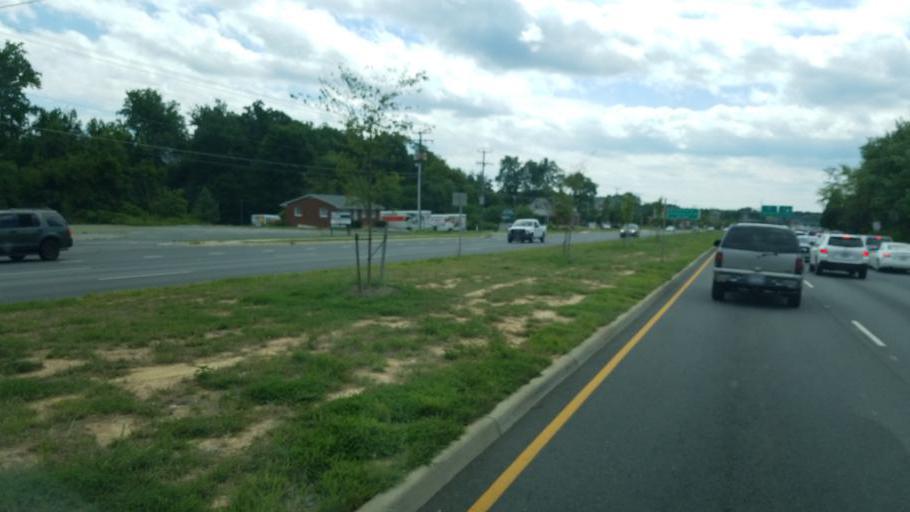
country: US
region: Virginia
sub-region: Stafford County
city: Falmouth
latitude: 38.3505
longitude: -77.5047
